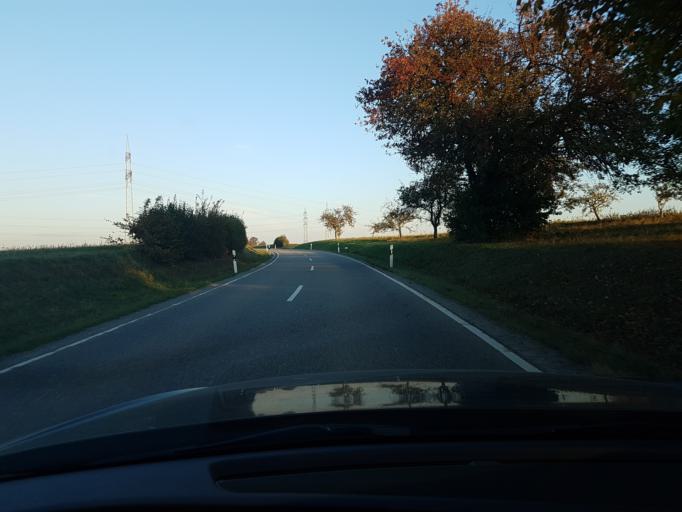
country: DE
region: Baden-Wuerttemberg
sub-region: Regierungsbezirk Stuttgart
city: Kirchheim am Neckar
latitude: 49.0559
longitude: 9.1190
